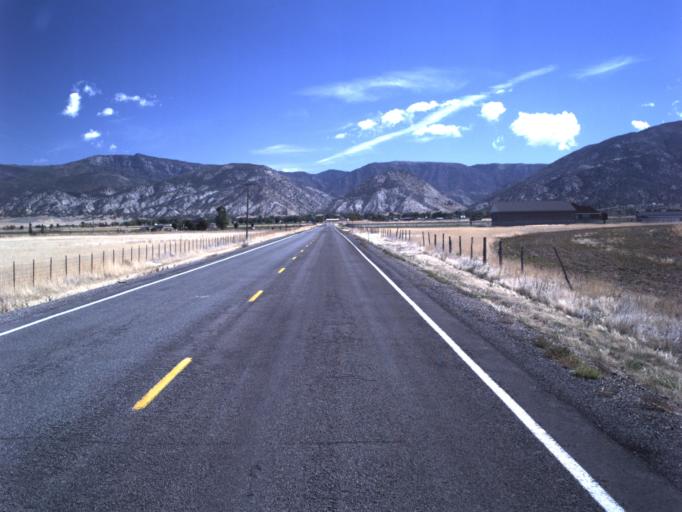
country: US
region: Utah
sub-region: Juab County
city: Nephi
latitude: 39.5580
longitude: -111.8958
